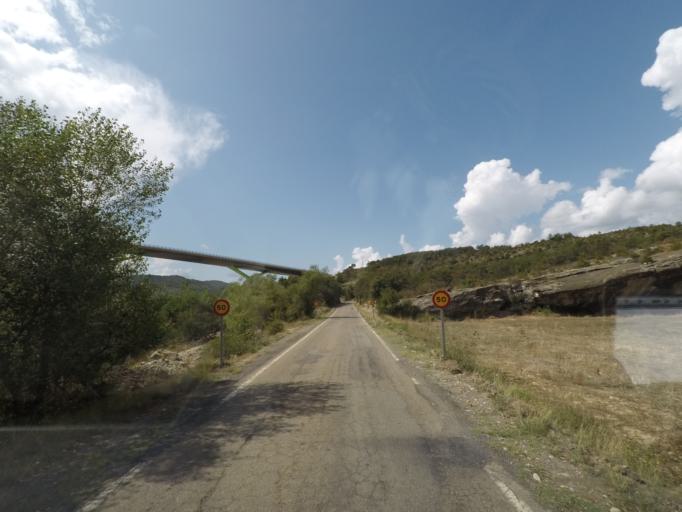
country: ES
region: Aragon
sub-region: Provincia de Huesca
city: Arguis
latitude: 42.4032
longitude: -0.3719
